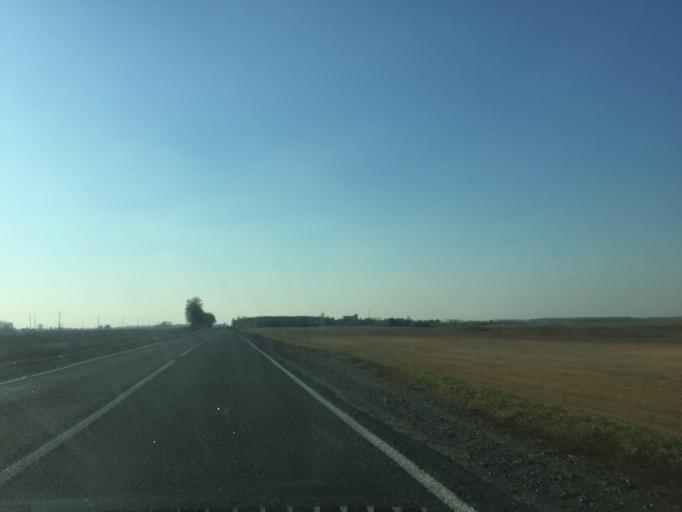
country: BY
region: Gomel
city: Dobrush
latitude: 52.3852
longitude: 31.4023
